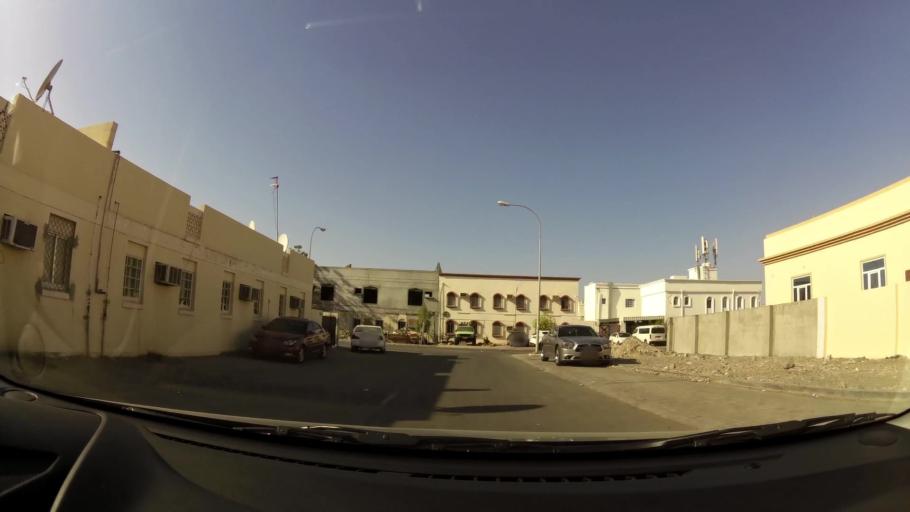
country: OM
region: Muhafazat Masqat
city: As Sib al Jadidah
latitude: 23.6233
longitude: 58.1930
